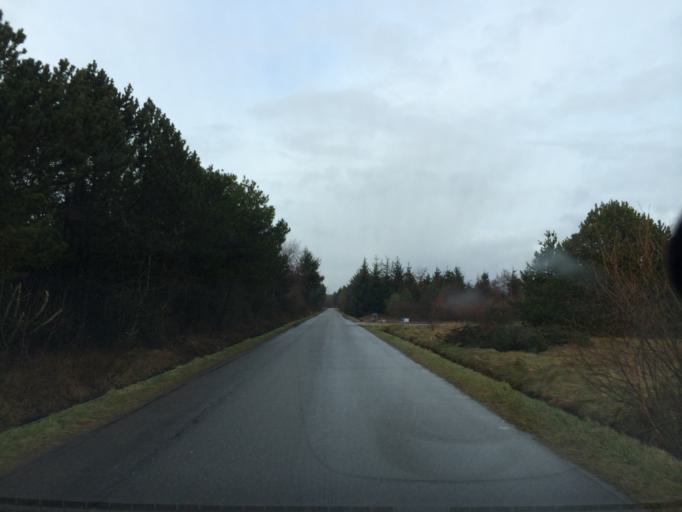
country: DK
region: Central Jutland
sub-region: Holstebro Kommune
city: Ulfborg
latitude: 56.2663
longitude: 8.1514
